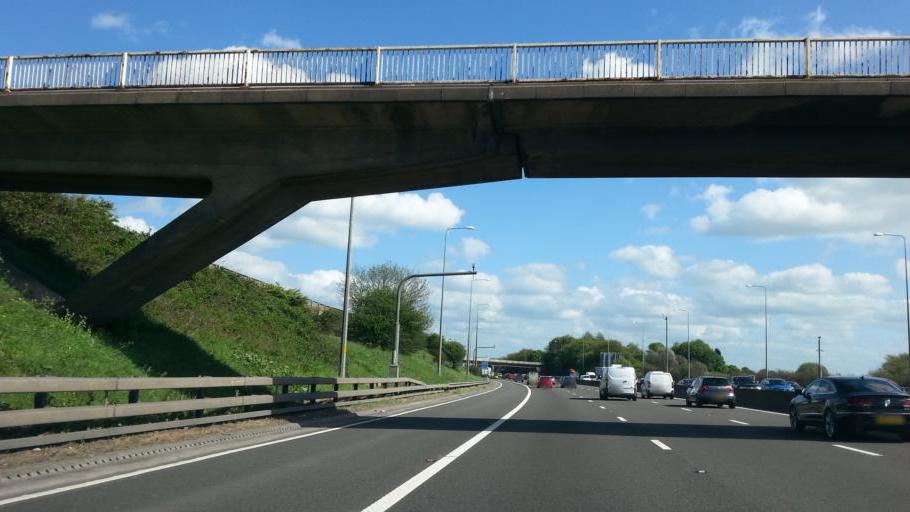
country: GB
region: England
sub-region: City and Borough of Leeds
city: Morley
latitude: 53.7363
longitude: -1.6196
